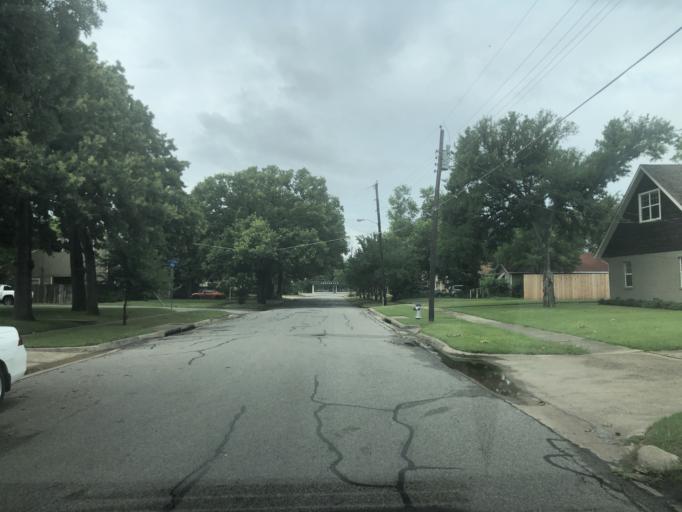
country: US
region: Texas
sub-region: Dallas County
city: Irving
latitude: 32.8100
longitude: -96.9450
